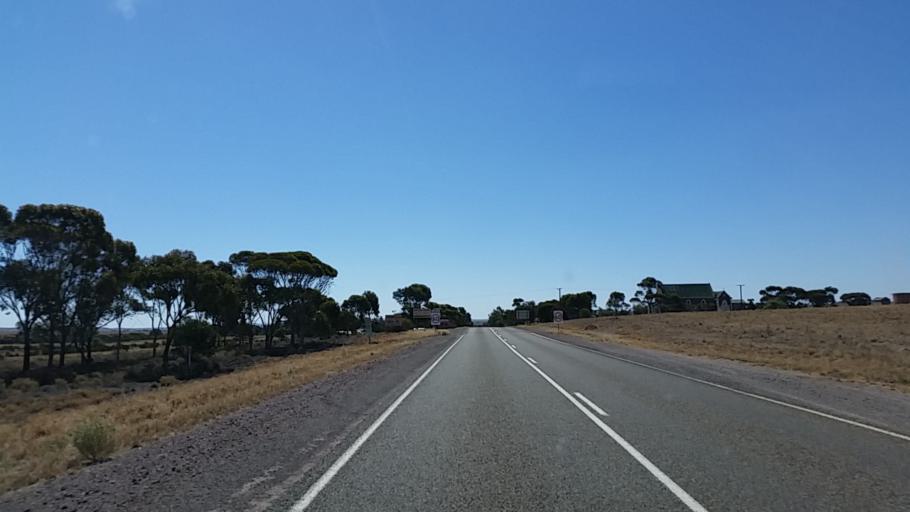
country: AU
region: South Australia
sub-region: Flinders Ranges
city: Quorn
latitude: -32.4292
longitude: 138.5314
